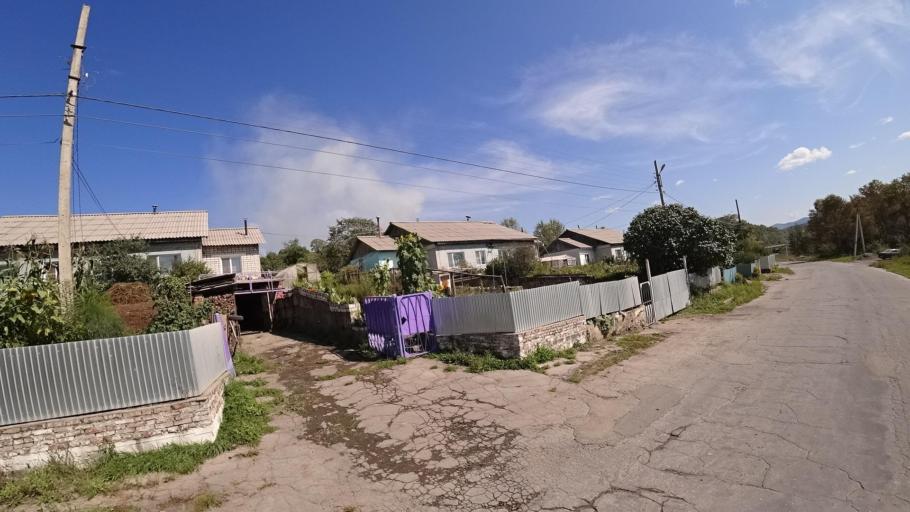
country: RU
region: Jewish Autonomous Oblast
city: Londoko
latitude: 49.0087
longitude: 131.8879
